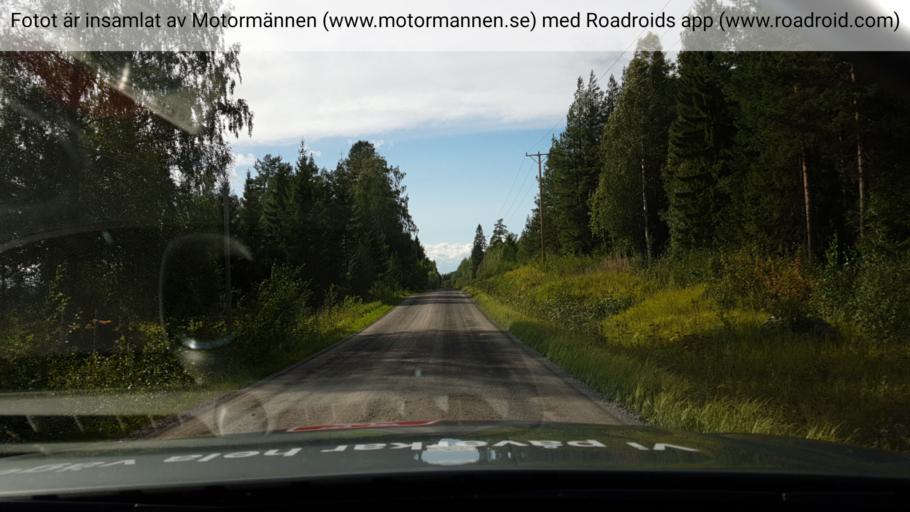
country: SE
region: Jaemtland
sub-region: Braecke Kommun
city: Braecke
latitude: 63.1957
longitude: 15.4935
